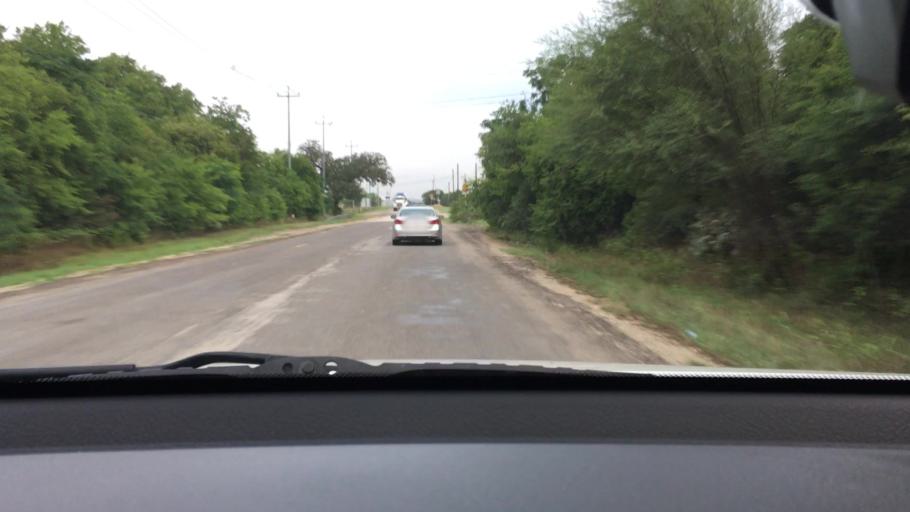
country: US
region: Texas
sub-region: Bexar County
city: Selma
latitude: 29.6059
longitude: -98.3294
